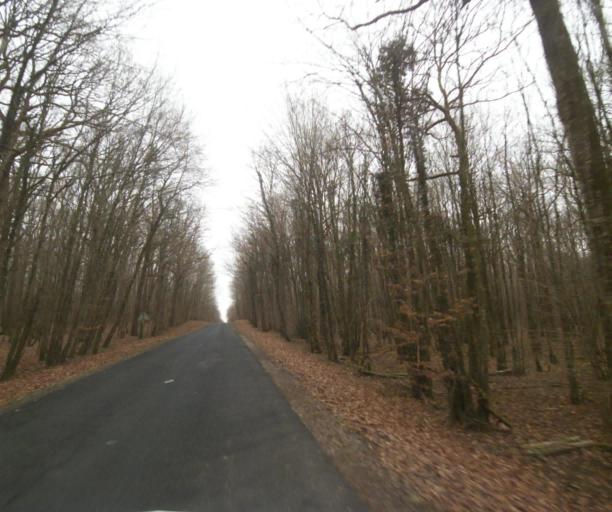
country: FR
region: Champagne-Ardenne
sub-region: Departement de la Haute-Marne
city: Bienville
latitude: 48.5622
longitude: 5.0050
